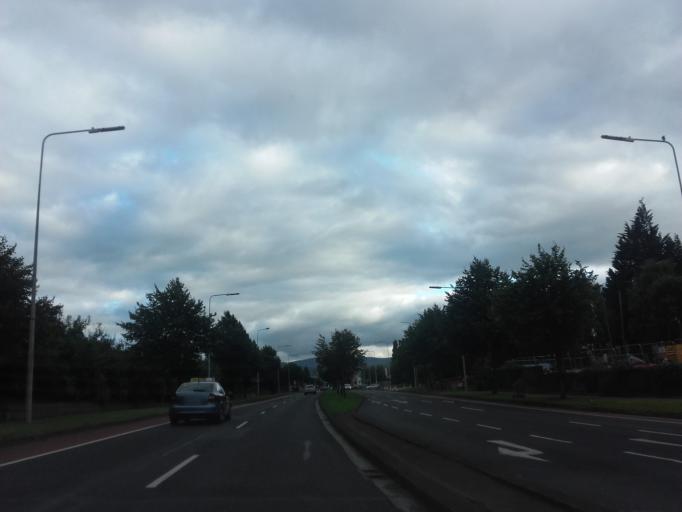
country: IE
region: Leinster
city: Tallaght
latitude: 53.2978
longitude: -6.3704
